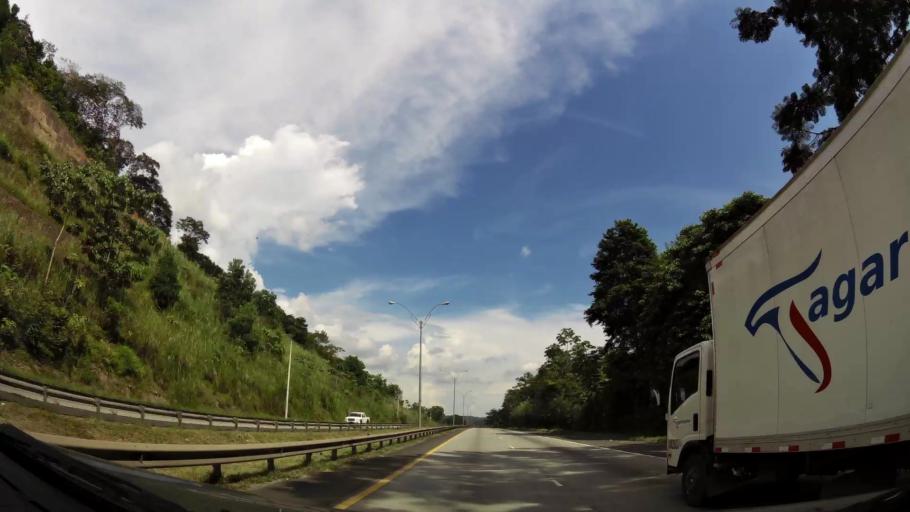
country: PA
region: Panama
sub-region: Distrito de Panama
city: Paraiso
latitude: 9.0272
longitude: -79.6048
